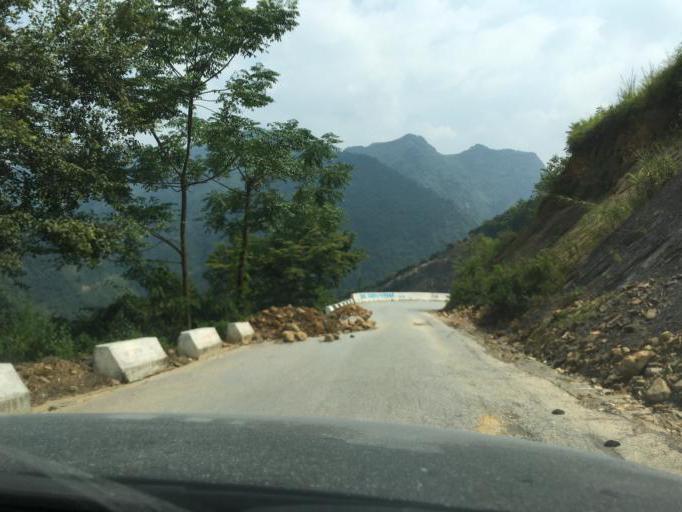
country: CN
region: Guangxi Zhuangzu Zizhiqu
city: Tongle
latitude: 25.2988
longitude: 106.2681
